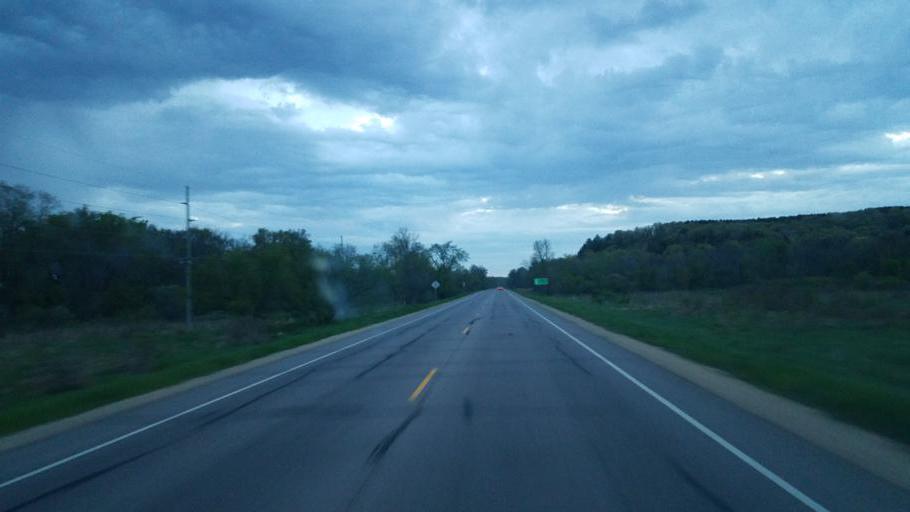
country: US
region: Wisconsin
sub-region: Juneau County
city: Elroy
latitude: 43.6891
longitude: -90.2662
